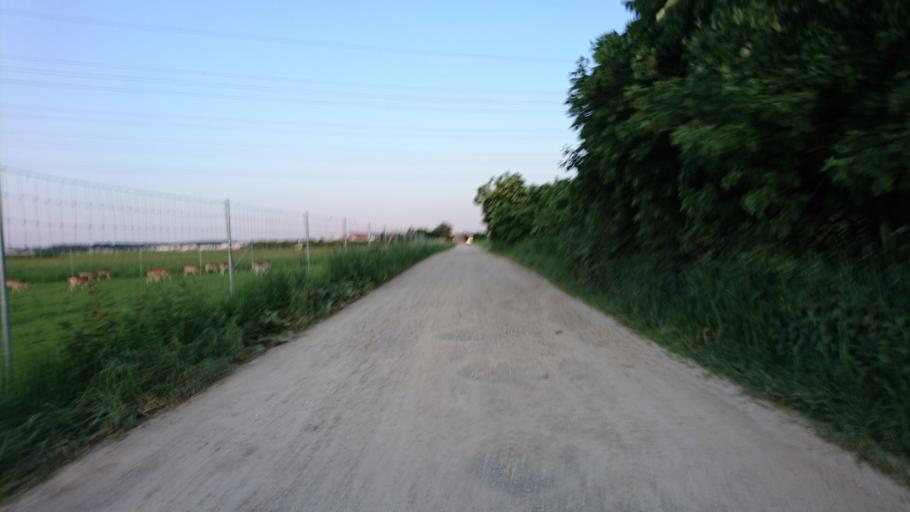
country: DE
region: Bavaria
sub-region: Upper Bavaria
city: Pliening
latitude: 48.1825
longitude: 11.7798
